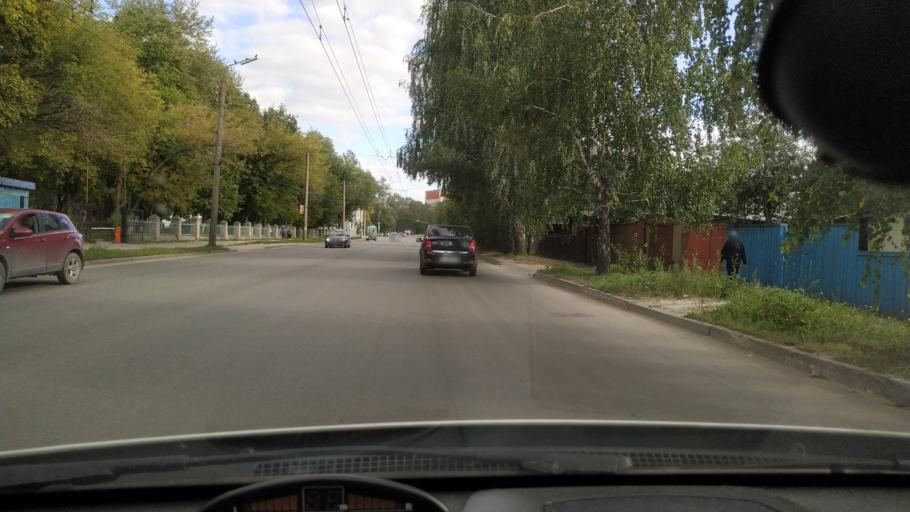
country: RU
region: Rjazan
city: Ryazan'
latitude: 54.6083
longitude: 39.7010
